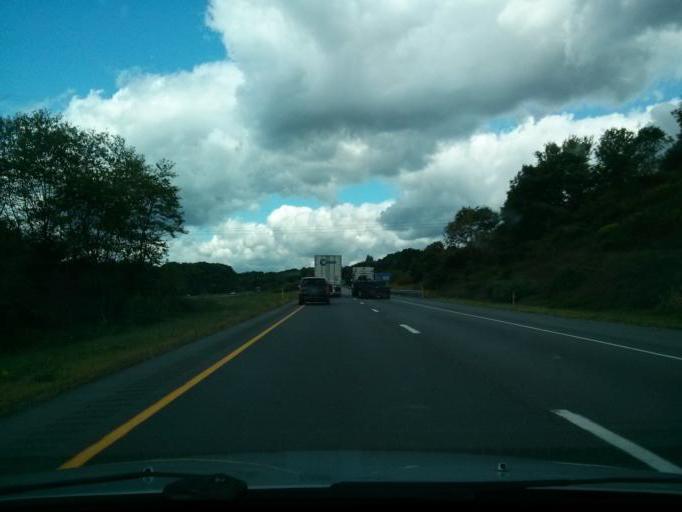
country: US
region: Pennsylvania
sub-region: Clearfield County
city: DuBois
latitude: 41.1436
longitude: -78.7501
